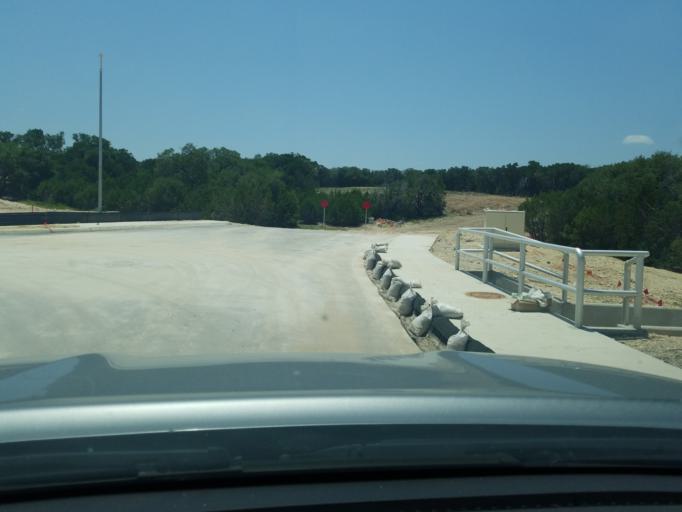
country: US
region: Texas
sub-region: Bexar County
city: Timberwood Park
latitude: 29.7062
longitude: -98.5048
